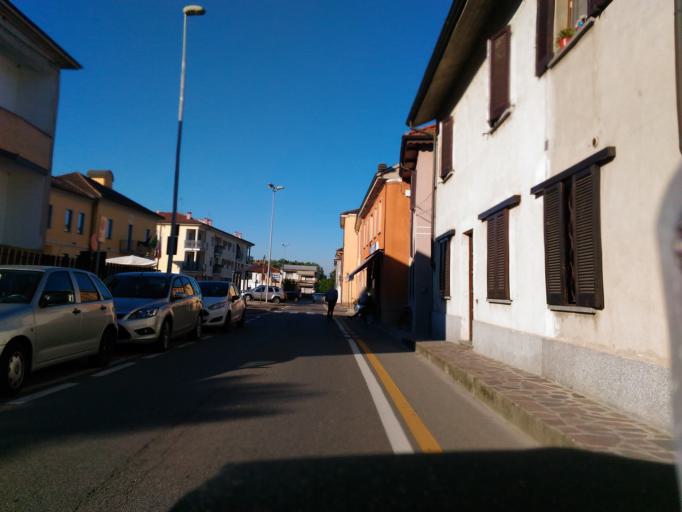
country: IT
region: Lombardy
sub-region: Provincia di Lodi
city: Salerano sul Lambro
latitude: 45.2946
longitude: 9.3875
